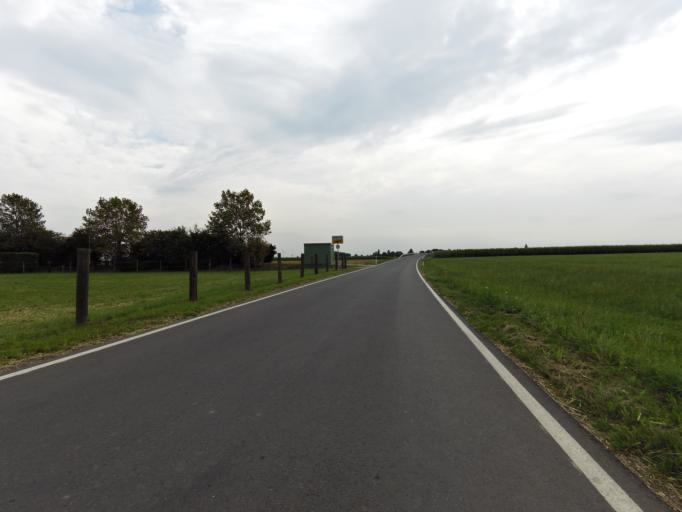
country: DE
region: North Rhine-Westphalia
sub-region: Regierungsbezirk Koln
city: Heinsberg
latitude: 51.0219
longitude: 6.0660
